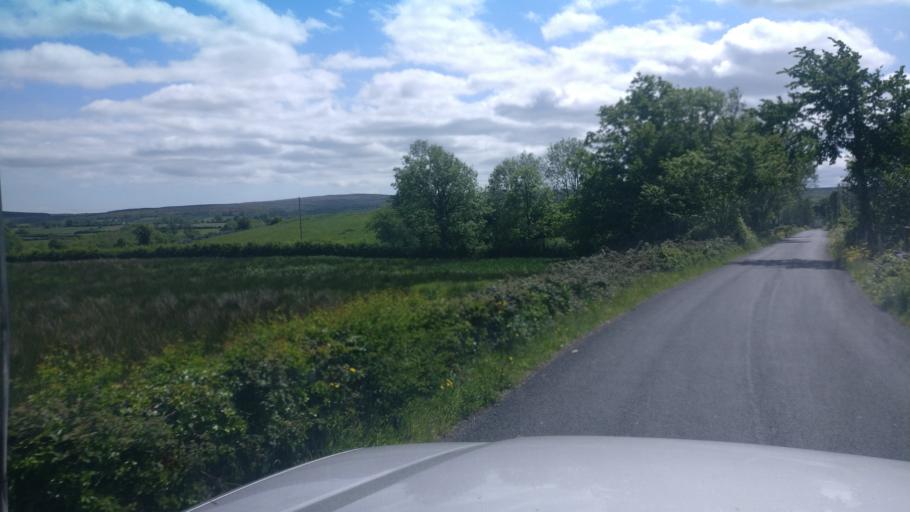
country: IE
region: Connaught
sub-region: County Galway
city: Gort
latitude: 53.1437
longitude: -8.7318
